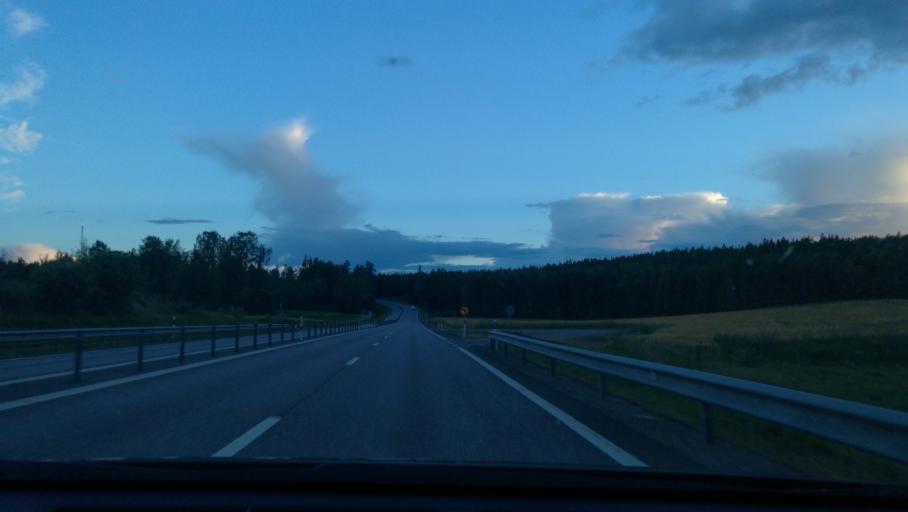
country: SE
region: Soedermanland
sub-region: Katrineholms Kommun
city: Katrineholm
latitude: 58.8446
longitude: 16.2005
